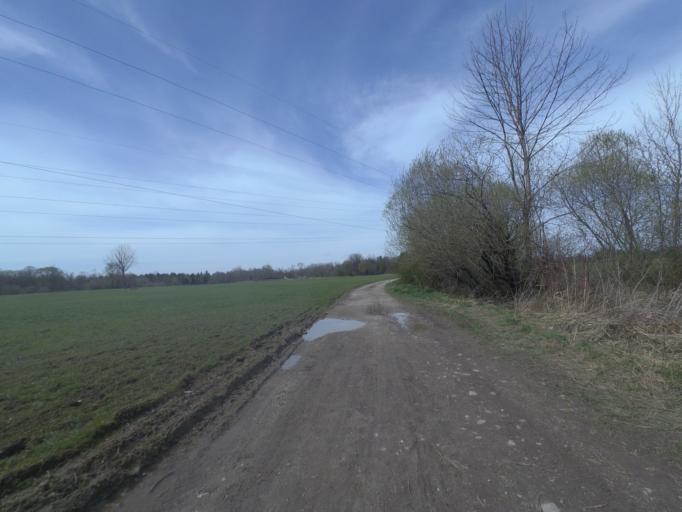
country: DE
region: Bavaria
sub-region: Upper Bavaria
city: Ainring
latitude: 47.8006
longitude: 12.9753
